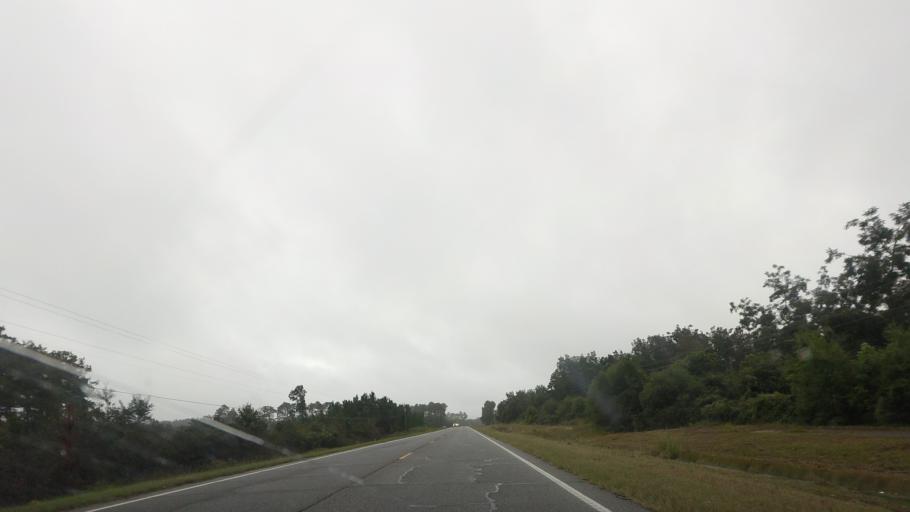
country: US
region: Georgia
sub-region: Ben Hill County
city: Fitzgerald
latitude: 31.7623
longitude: -83.2454
